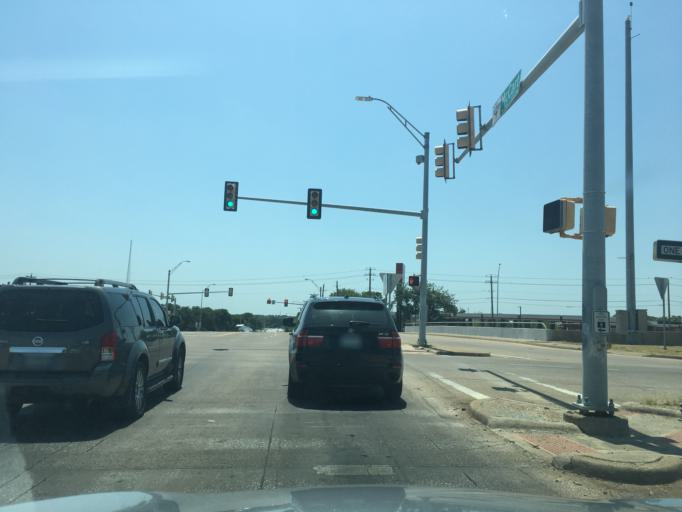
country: US
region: Texas
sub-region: Tarrant County
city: Edgecliff Village
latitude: 32.6687
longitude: -97.3560
